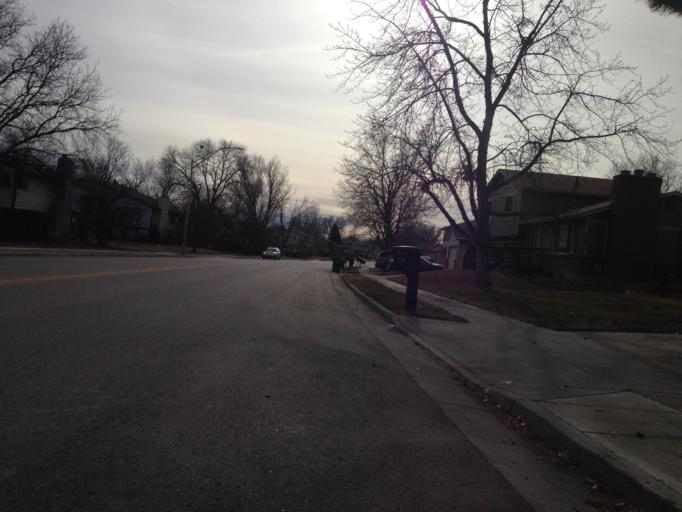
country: US
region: Colorado
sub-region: Adams County
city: Westminster
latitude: 39.8506
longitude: -105.0641
